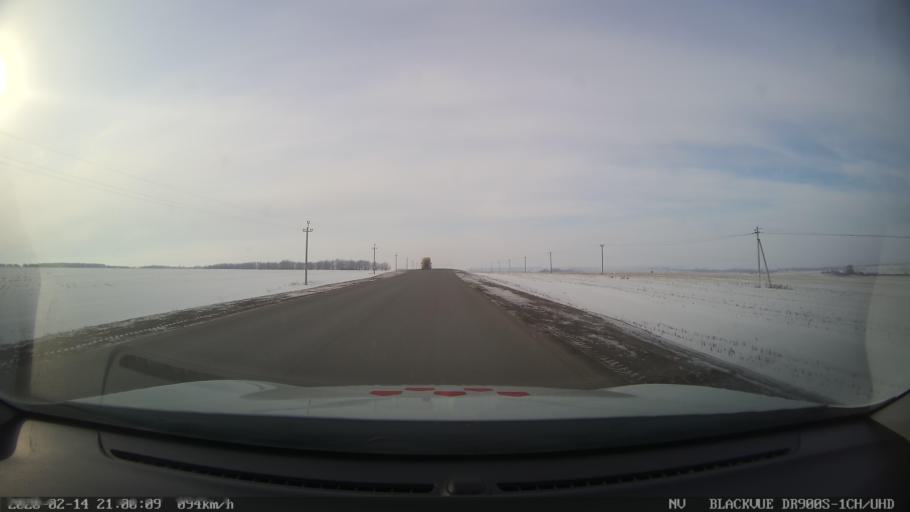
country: RU
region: Tatarstan
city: Kuybyshevskiy Zaton
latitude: 55.1732
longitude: 49.2257
